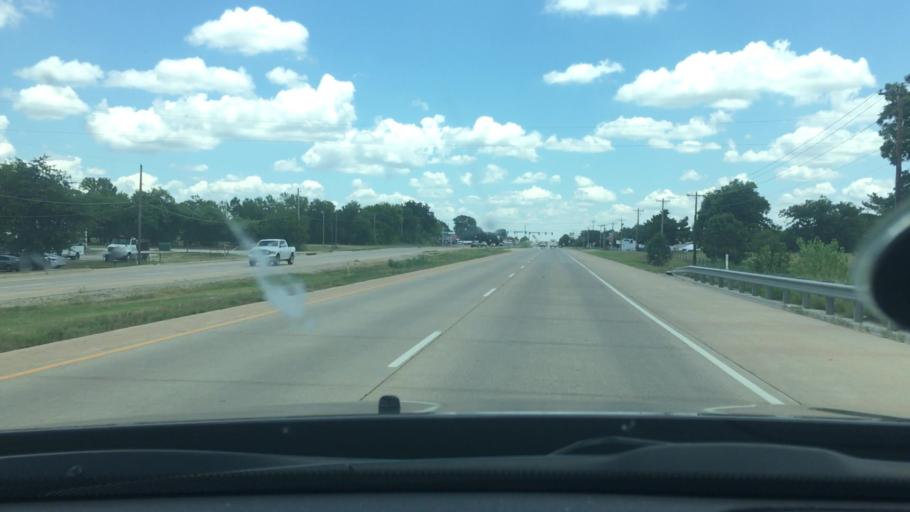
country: US
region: Oklahoma
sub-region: Carter County
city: Lone Grove
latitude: 34.1727
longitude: -97.2350
